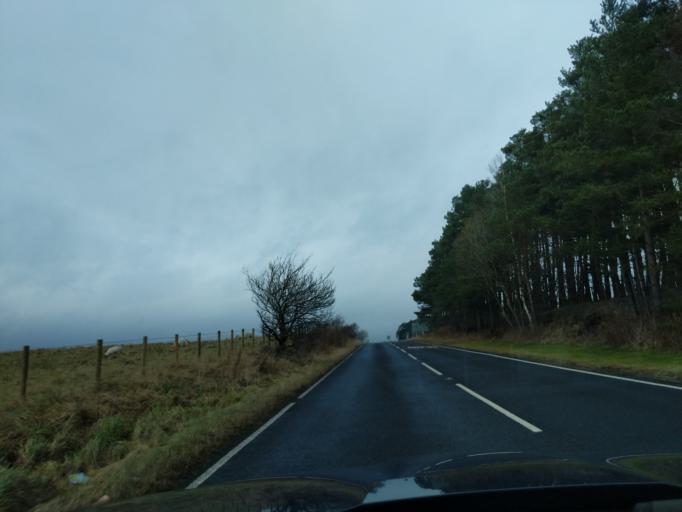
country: GB
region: England
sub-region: Northumberland
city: Rothley
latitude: 55.1667
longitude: -2.0201
